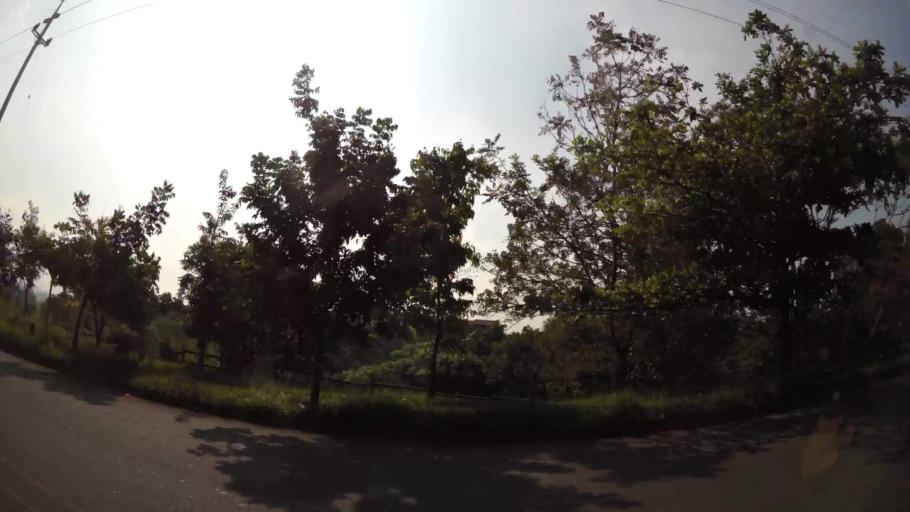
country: CO
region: Antioquia
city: La Estrella
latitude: 6.1701
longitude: -75.6333
